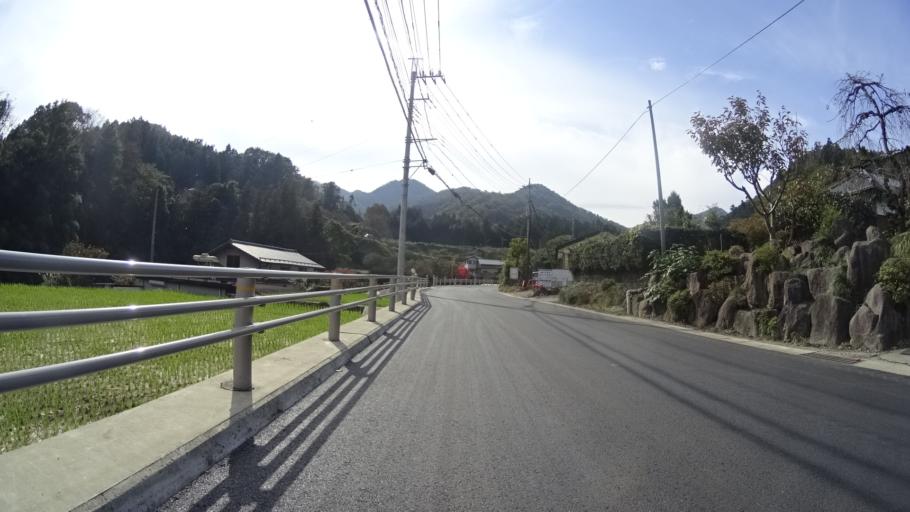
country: JP
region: Yamanashi
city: Otsuki
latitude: 35.6000
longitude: 138.9751
